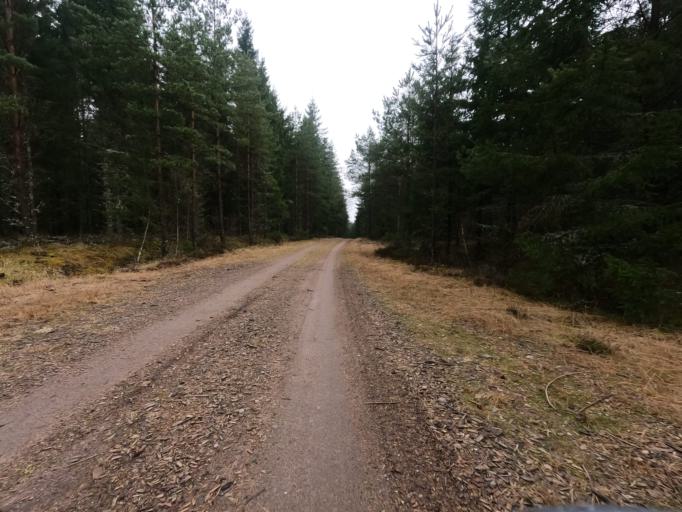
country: SE
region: Kronoberg
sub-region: Markaryds Kommun
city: Stromsnasbruk
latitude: 56.8060
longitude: 13.5708
